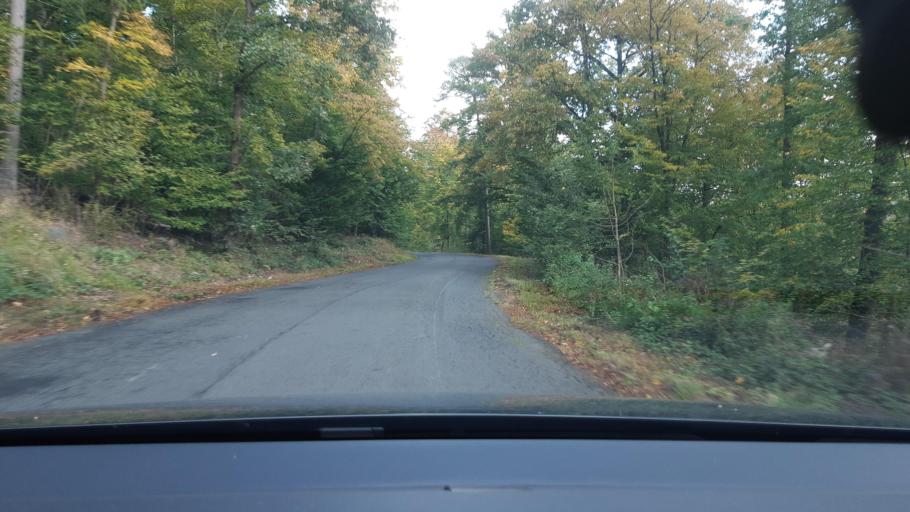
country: DE
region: Hesse
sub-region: Regierungsbezirk Giessen
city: Merkenbach
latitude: 50.6647
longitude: 8.3004
